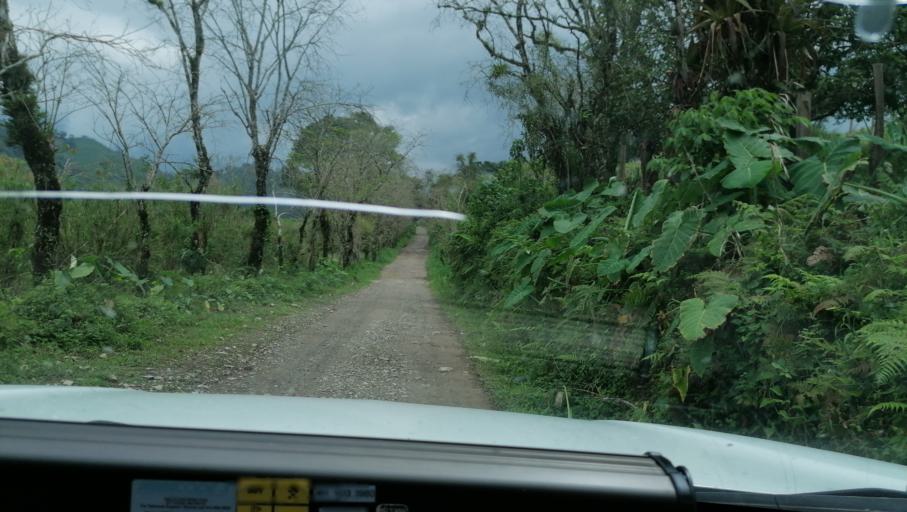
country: MX
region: Chiapas
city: Ixtacomitan
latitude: 17.3451
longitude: -93.1364
